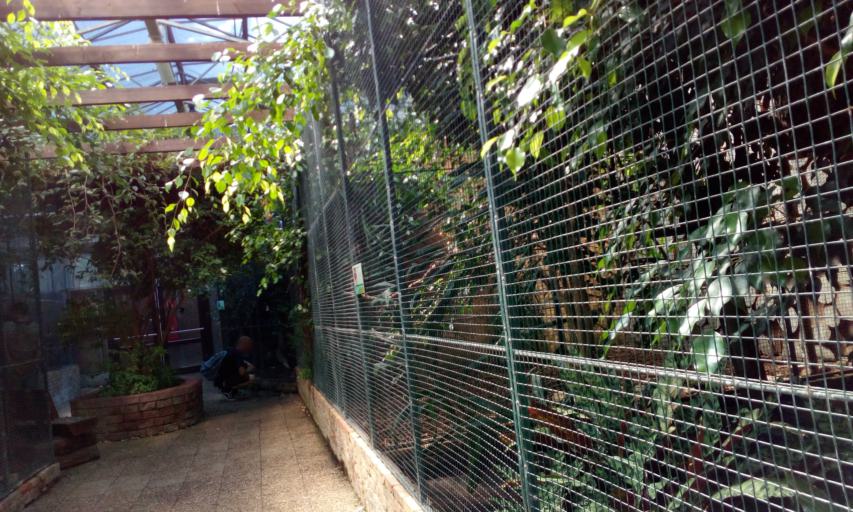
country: NL
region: South Holland
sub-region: Gemeente Alphen aan den Rijn
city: Alphen aan den Rijn
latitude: 52.1406
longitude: 4.6505
